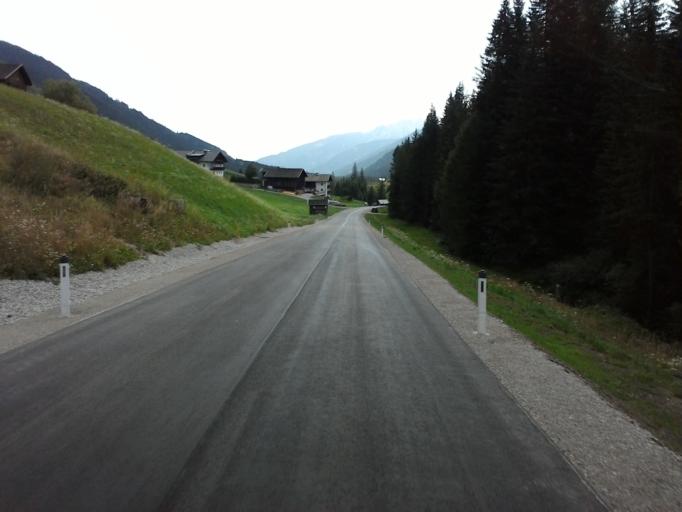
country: AT
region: Tyrol
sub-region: Politischer Bezirk Lienz
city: Abfaltersbach
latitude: 46.7154
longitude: 12.5585
